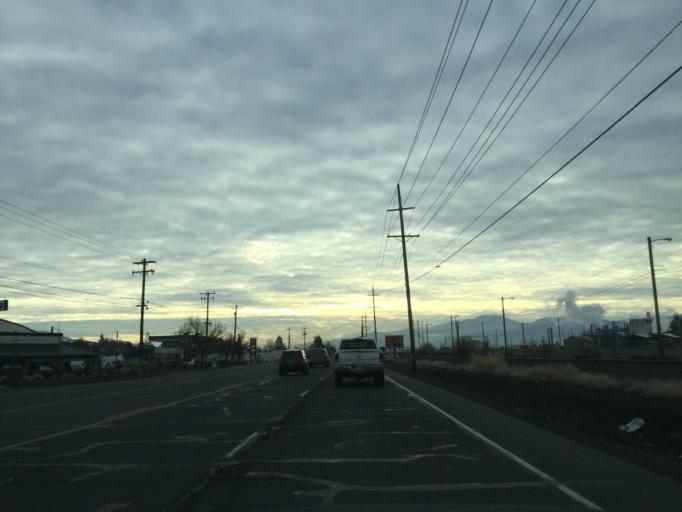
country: US
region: Oregon
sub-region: Jackson County
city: Central Point
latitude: 42.3610
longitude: -122.9065
